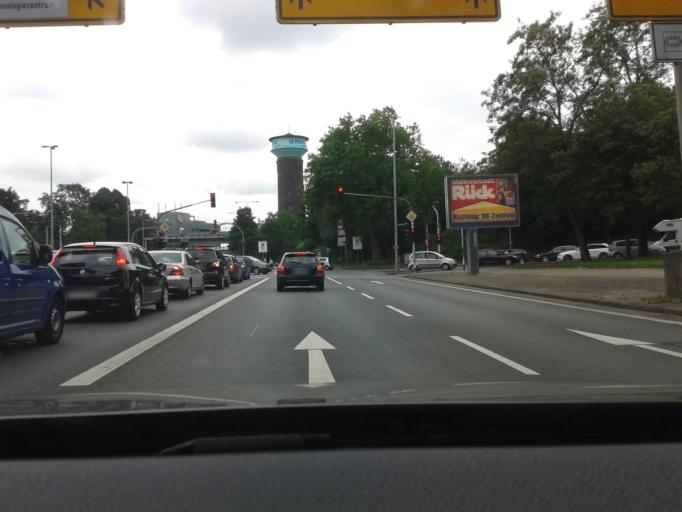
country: DE
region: North Rhine-Westphalia
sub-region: Regierungsbezirk Dusseldorf
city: Oberhausen
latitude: 51.4885
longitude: 6.8626
